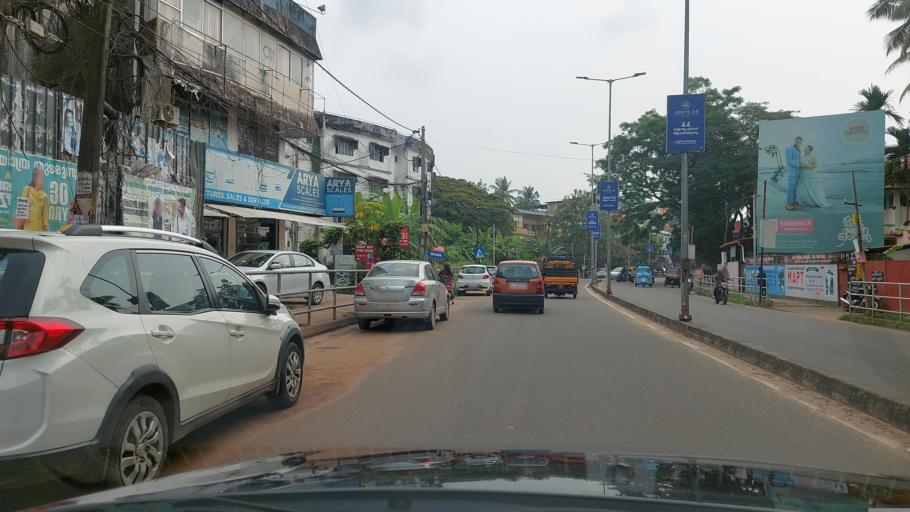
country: IN
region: Kerala
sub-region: Kozhikode
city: Kozhikode
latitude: 11.2546
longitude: 75.7865
